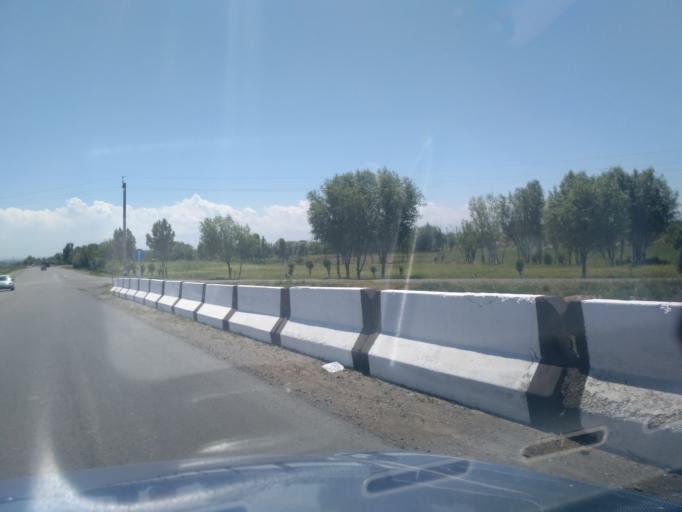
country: UZ
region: Sirdaryo
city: Yangiyer
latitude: 40.2376
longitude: 68.8449
